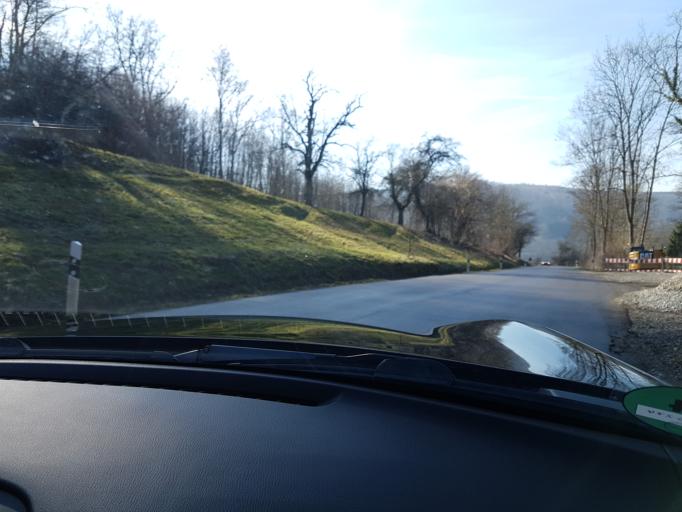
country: DE
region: Baden-Wuerttemberg
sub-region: Regierungsbezirk Stuttgart
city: Langenburg
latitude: 49.2472
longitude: 9.8584
